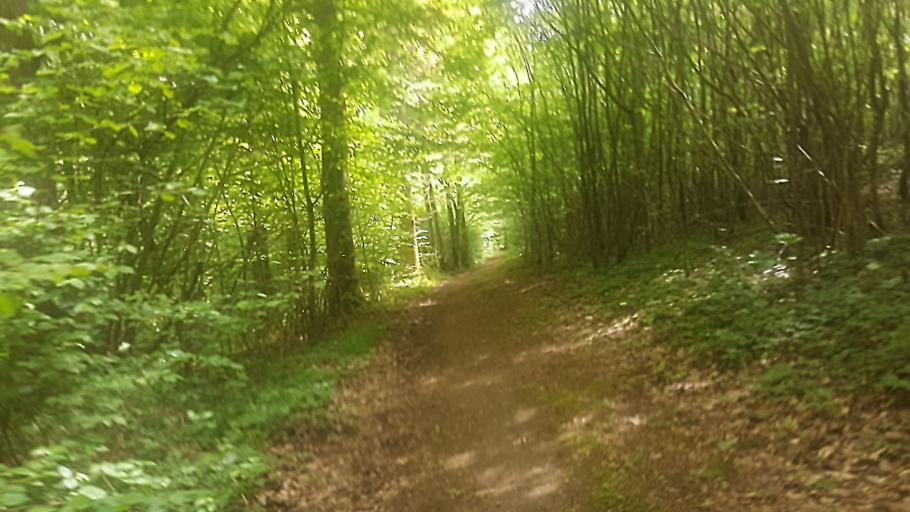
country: FR
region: Champagne-Ardenne
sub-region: Departement des Ardennes
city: Haybes
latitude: 50.0546
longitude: 4.6070
